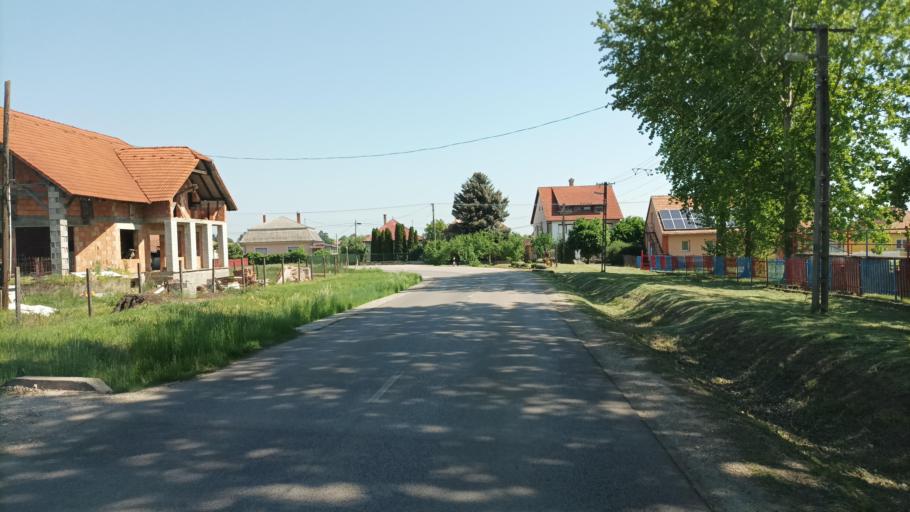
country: HU
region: Pest
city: Uri
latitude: 47.4100
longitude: 19.5247
